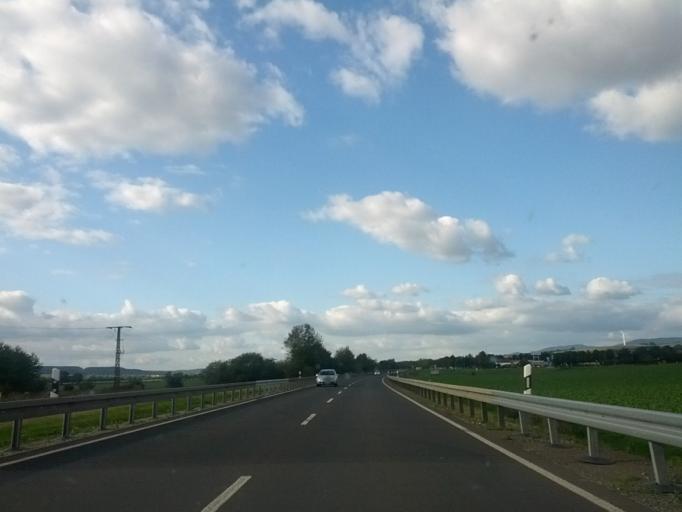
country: DE
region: Thuringia
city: Fambach
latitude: 50.7317
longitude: 10.3636
